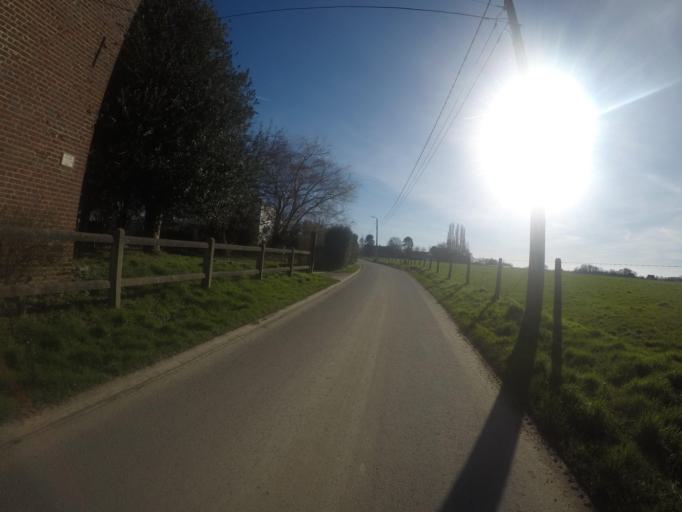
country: BE
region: Flanders
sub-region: Provincie Vlaams-Brabant
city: Pepingen
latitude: 50.7381
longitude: 4.1659
